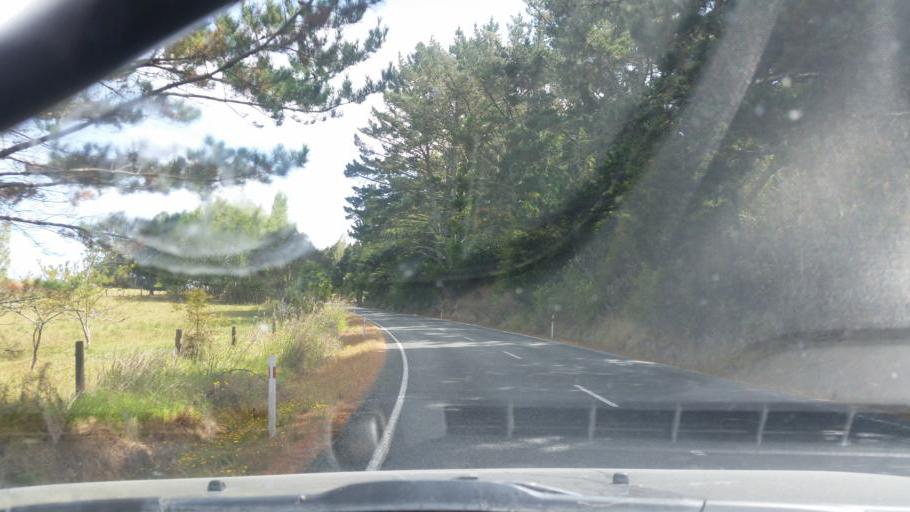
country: NZ
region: Northland
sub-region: Whangarei
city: Ruakaka
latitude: -35.9490
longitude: 174.2938
